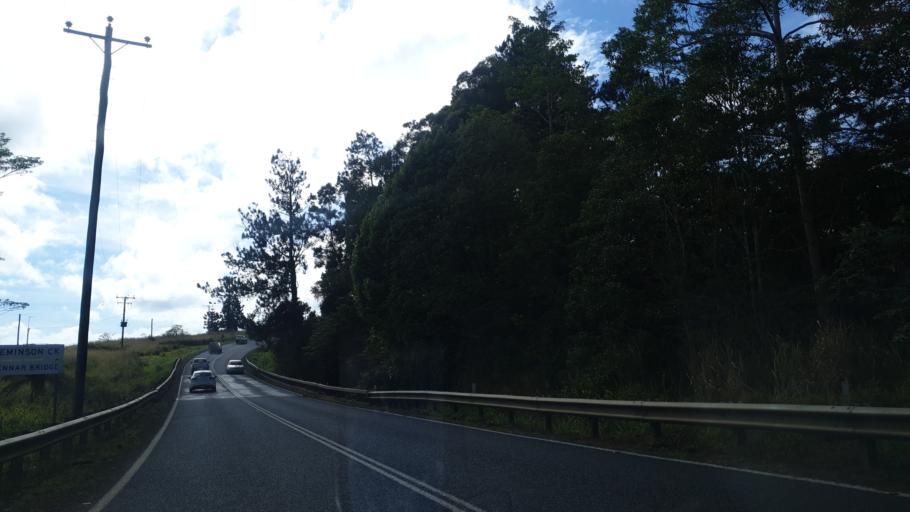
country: AU
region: Queensland
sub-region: Tablelands
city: Atherton
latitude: -17.3457
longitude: 145.5767
